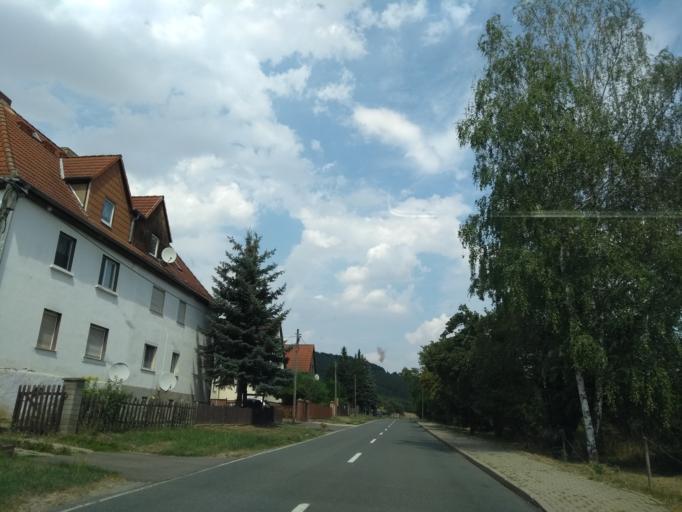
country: DE
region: Saxony-Anhalt
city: Wetterzeube
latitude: 51.0105
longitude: 12.0142
